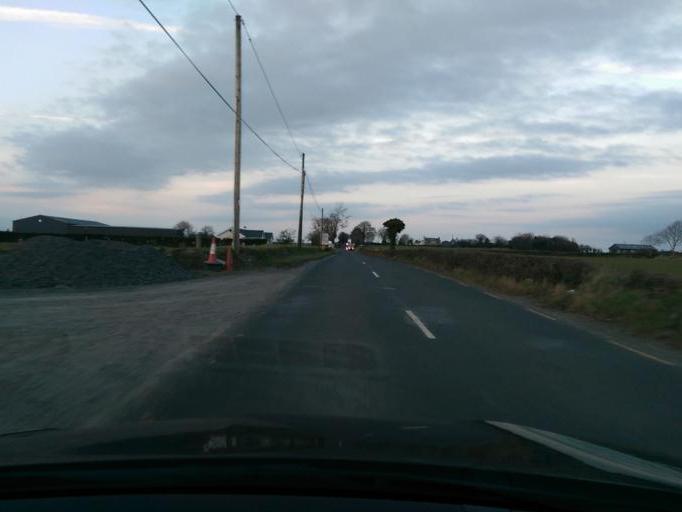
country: IE
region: Connaught
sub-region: County Galway
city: Portumna
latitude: 53.0440
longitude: -8.1114
